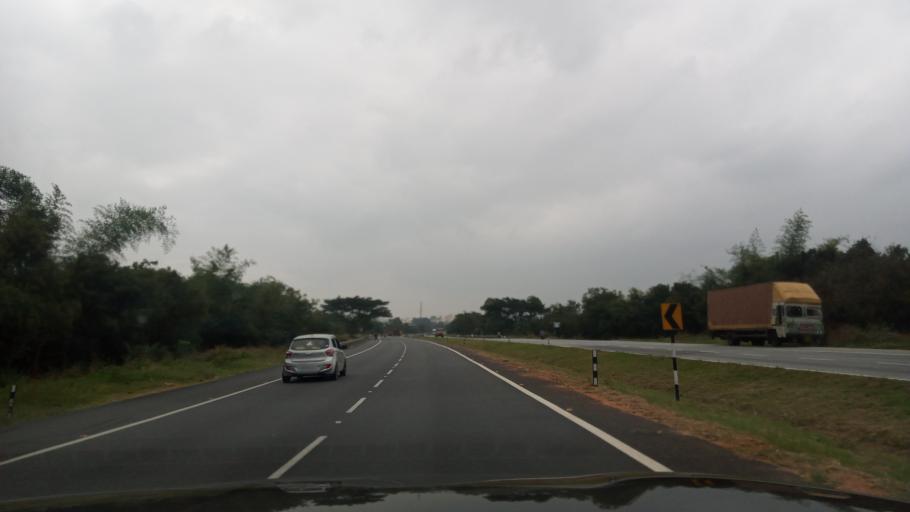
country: IN
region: Karnataka
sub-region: Bangalore Rural
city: Nelamangala
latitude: 13.0232
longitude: 77.4756
